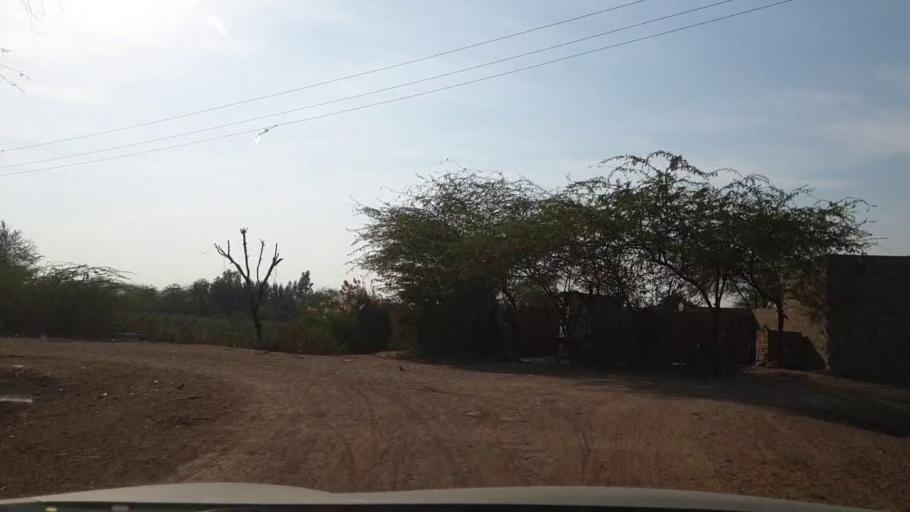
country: PK
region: Sindh
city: Berani
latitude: 25.7154
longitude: 68.8049
